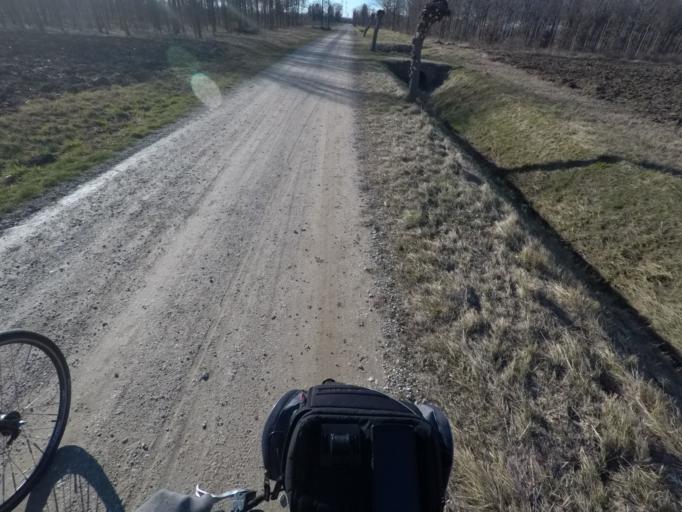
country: IT
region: Friuli Venezia Giulia
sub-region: Provincia di Udine
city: Remanzacco
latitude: 46.0967
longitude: 13.3369
